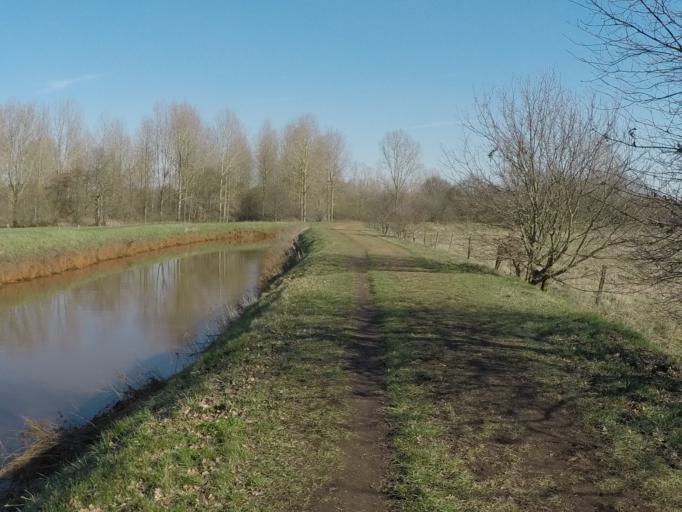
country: BE
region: Flanders
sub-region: Provincie Antwerpen
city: Herenthout
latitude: 51.1217
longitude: 4.7222
